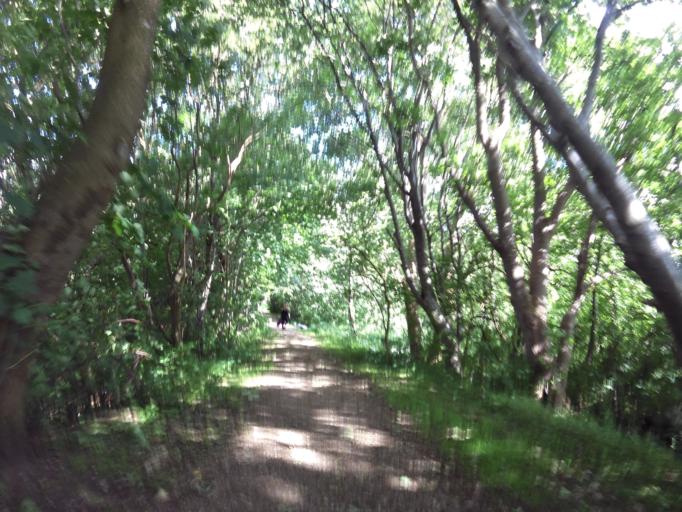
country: DK
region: South Denmark
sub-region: Kolding Kommune
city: Vamdrup
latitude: 55.3588
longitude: 9.2006
